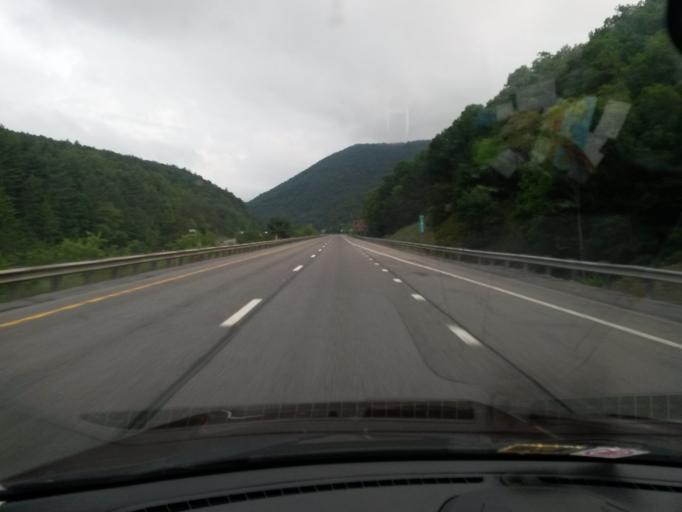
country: US
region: West Virginia
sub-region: Greenbrier County
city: White Sulphur Springs
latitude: 37.7847
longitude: -80.2399
